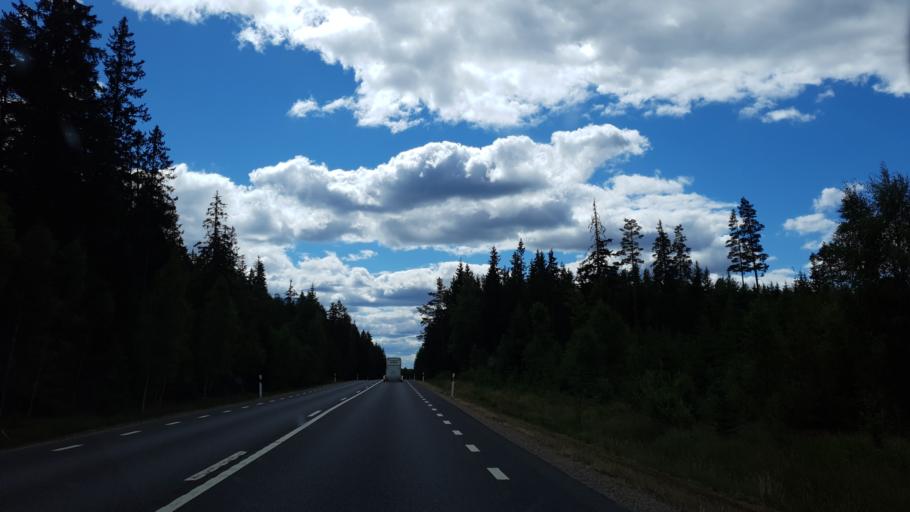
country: SE
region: Joenkoeping
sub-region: Vetlanda Kommun
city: Vetlanda
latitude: 57.2497
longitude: 15.1358
